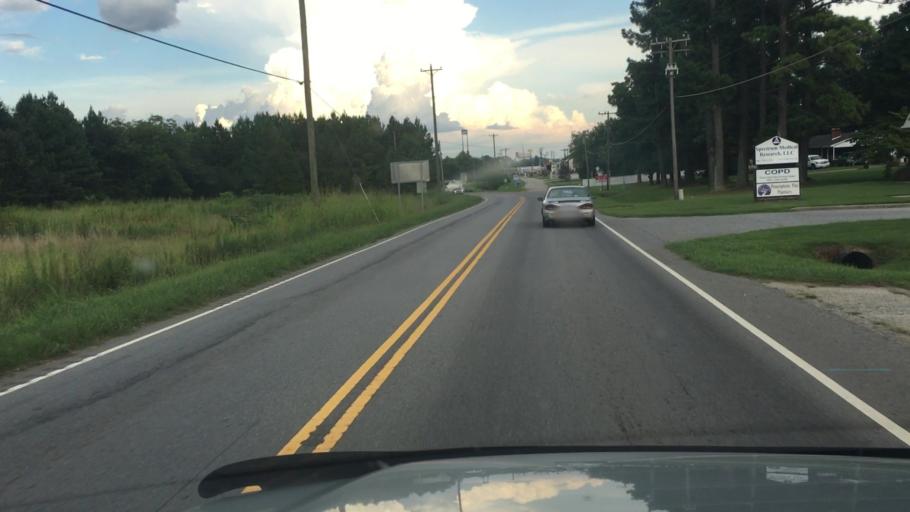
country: US
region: South Carolina
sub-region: Cherokee County
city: Gaffney
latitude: 35.1012
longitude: -81.6771
